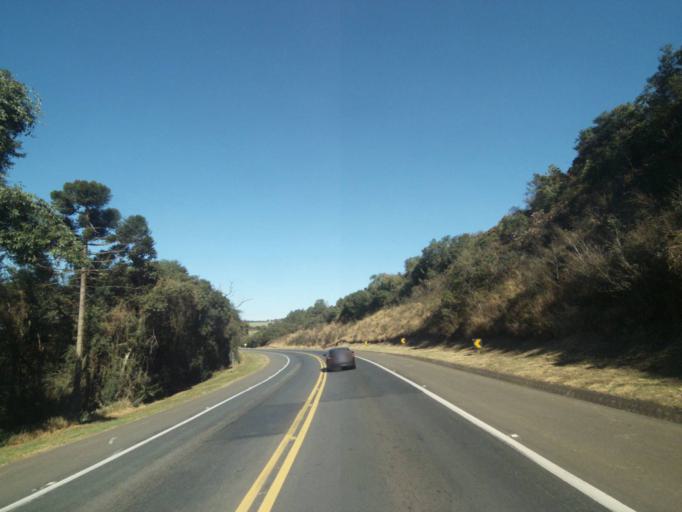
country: BR
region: Parana
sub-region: Tibagi
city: Tibagi
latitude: -24.7292
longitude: -50.5384
